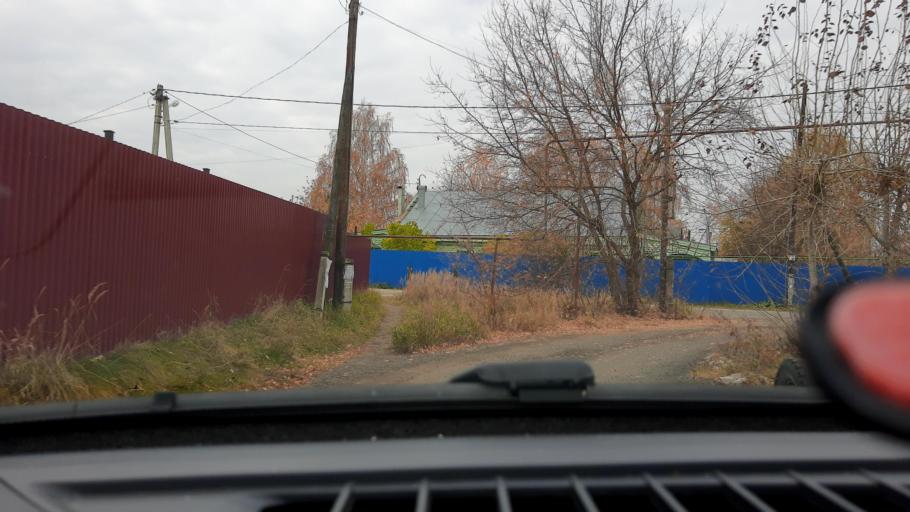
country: RU
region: Nizjnij Novgorod
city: Gorbatovka
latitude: 56.3287
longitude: 43.8340
